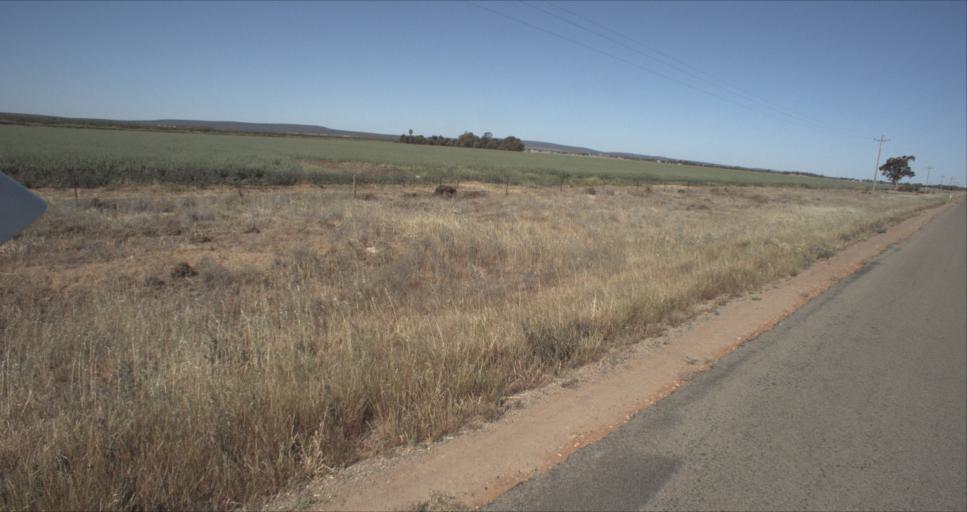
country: AU
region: New South Wales
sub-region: Leeton
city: Leeton
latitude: -34.4817
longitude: 146.3722
